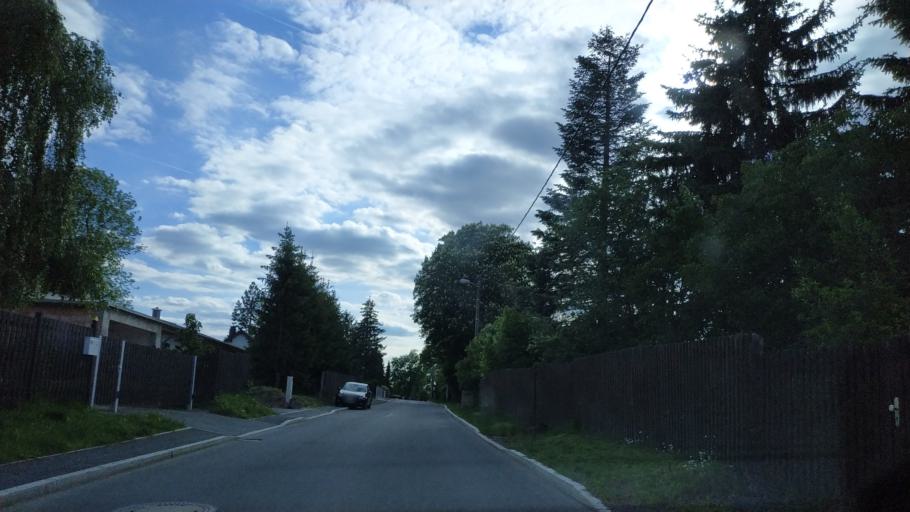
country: DE
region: Saxony
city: Pohl
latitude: 50.5472
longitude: 12.1456
